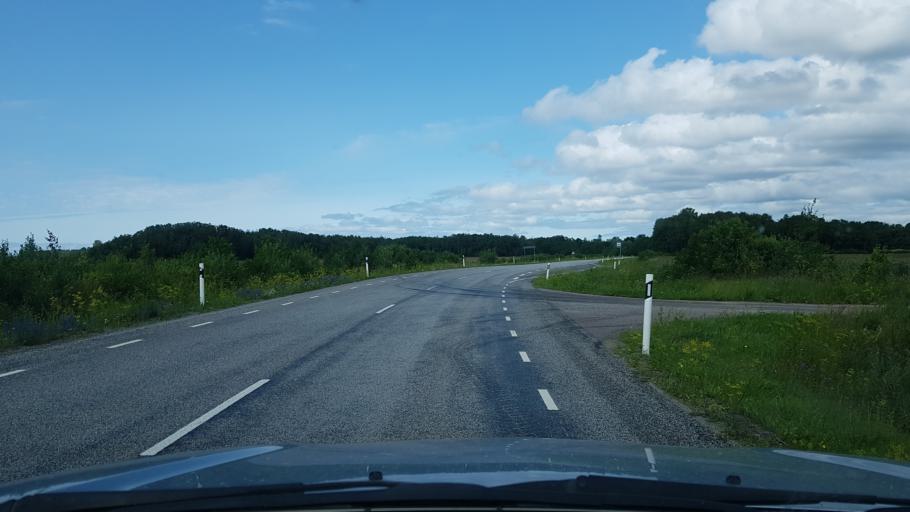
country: EE
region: Ida-Virumaa
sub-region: Narva-Joesuu linn
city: Narva-Joesuu
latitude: 59.3700
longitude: 27.9290
